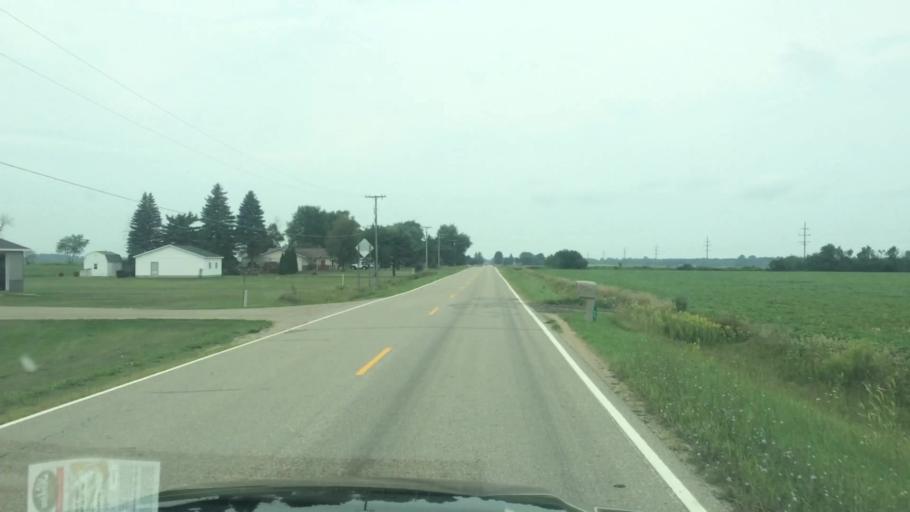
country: US
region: Michigan
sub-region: Huron County
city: Bad Axe
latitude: 44.0036
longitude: -83.0101
